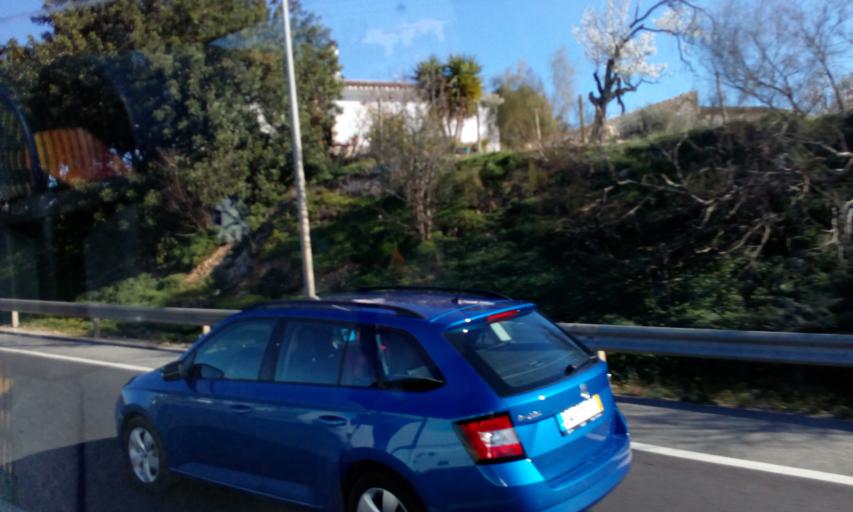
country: PT
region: Faro
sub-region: Faro
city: Santa Barbara de Nexe
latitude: 37.0738
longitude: -7.9784
